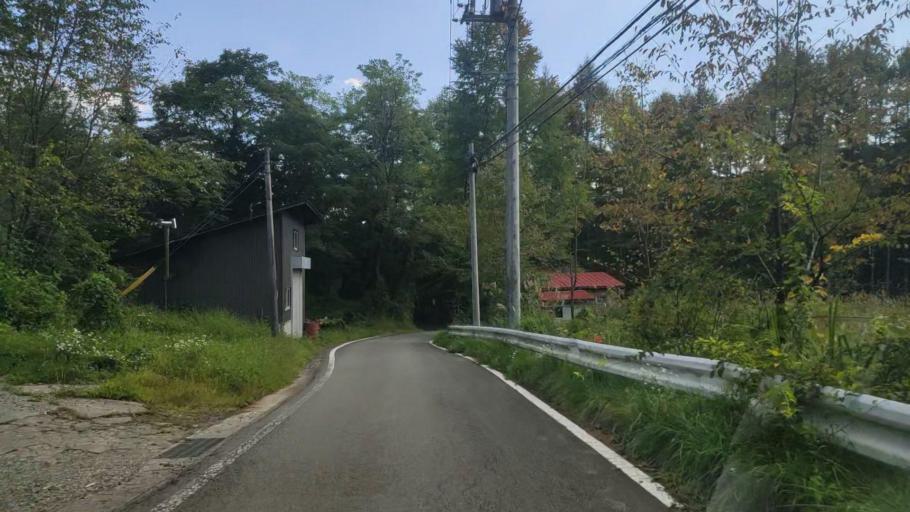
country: JP
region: Gunma
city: Nakanojomachi
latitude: 36.6572
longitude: 138.6302
